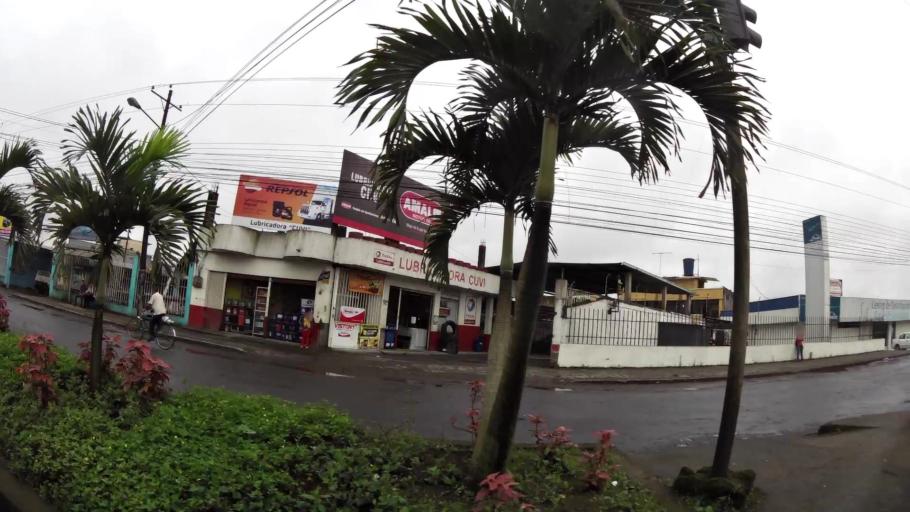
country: EC
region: Santo Domingo de los Tsachilas
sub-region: Canton Santo Domingo de los Colorados
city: Santo Domingo de los Colorados
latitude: -0.2659
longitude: -79.1919
